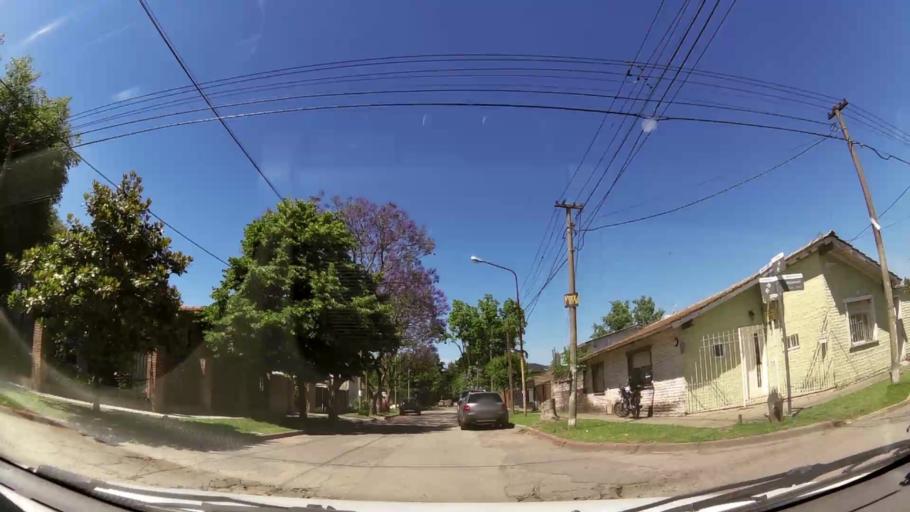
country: AR
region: Buenos Aires
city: Ituzaingo
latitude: -34.6784
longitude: -58.6593
